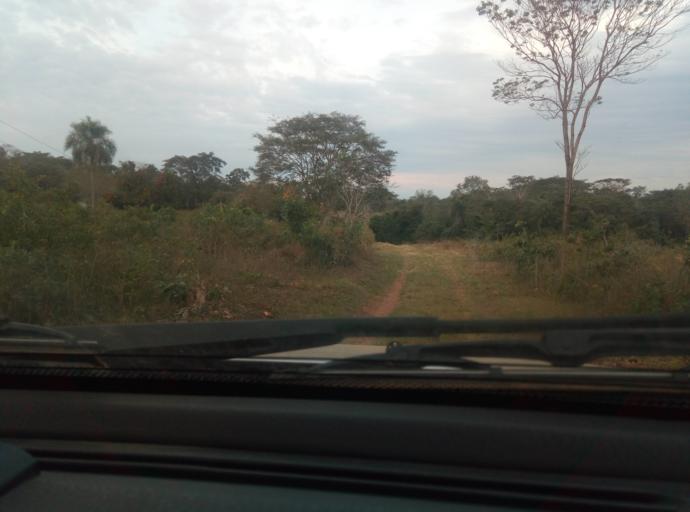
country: PY
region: Caaguazu
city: Carayao
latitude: -25.1460
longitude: -56.3957
